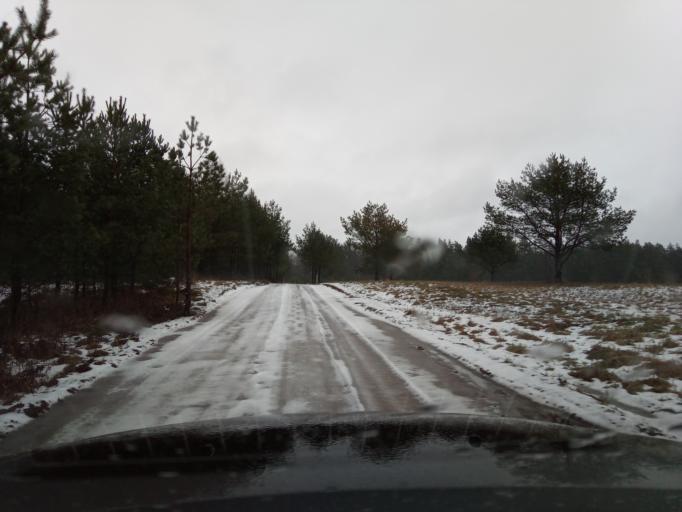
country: LT
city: Svencioneliai
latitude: 55.3357
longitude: 25.8048
